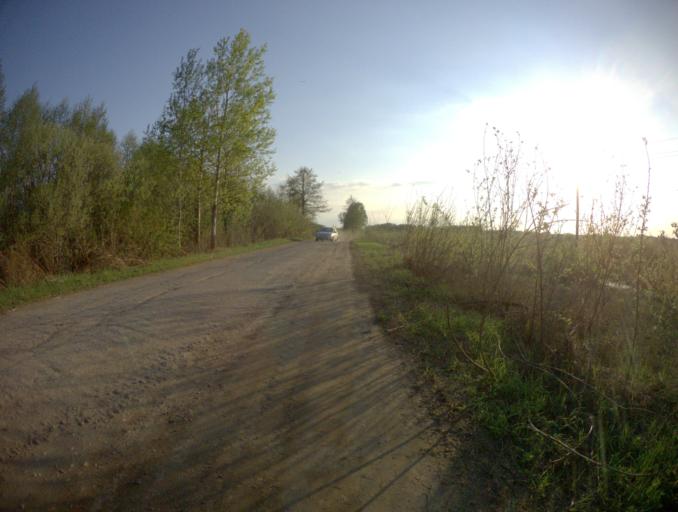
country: RU
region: Vladimir
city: Vyazniki
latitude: 56.3188
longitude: 42.1055
